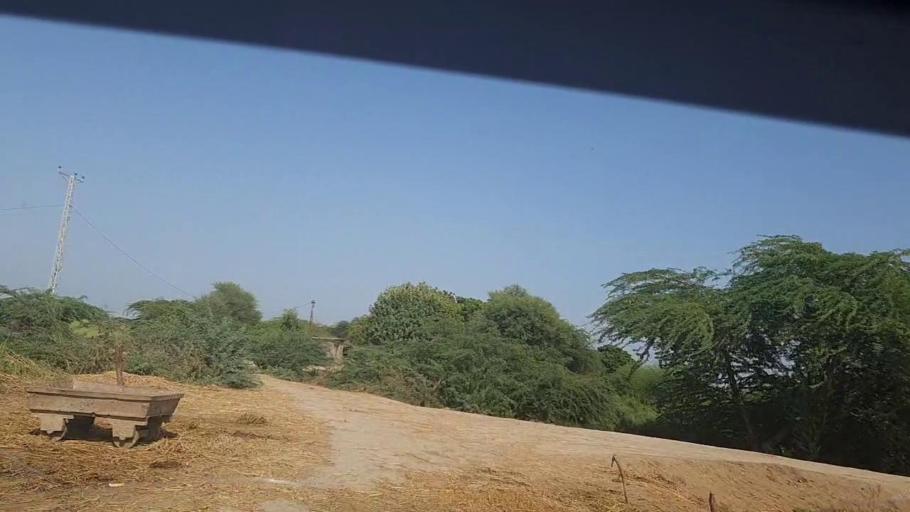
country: PK
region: Sindh
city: Rajo Khanani
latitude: 24.9550
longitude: 68.8979
